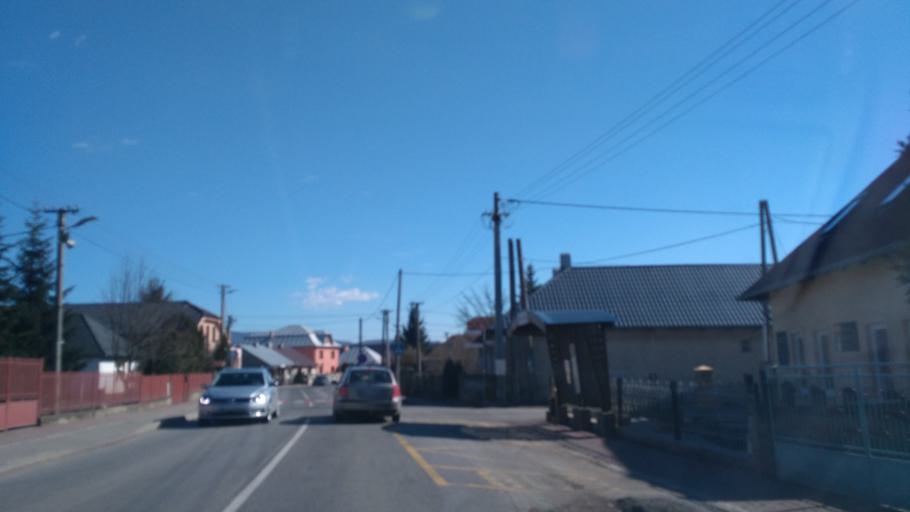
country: SK
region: Kosicky
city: Kosice
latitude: 48.6312
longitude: 21.3030
